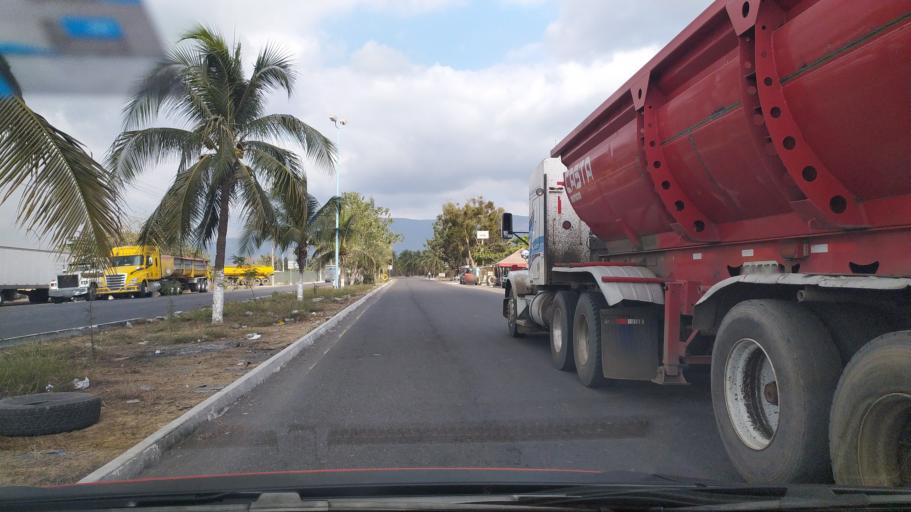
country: MX
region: Colima
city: Tecoman
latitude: 18.9404
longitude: -103.8937
